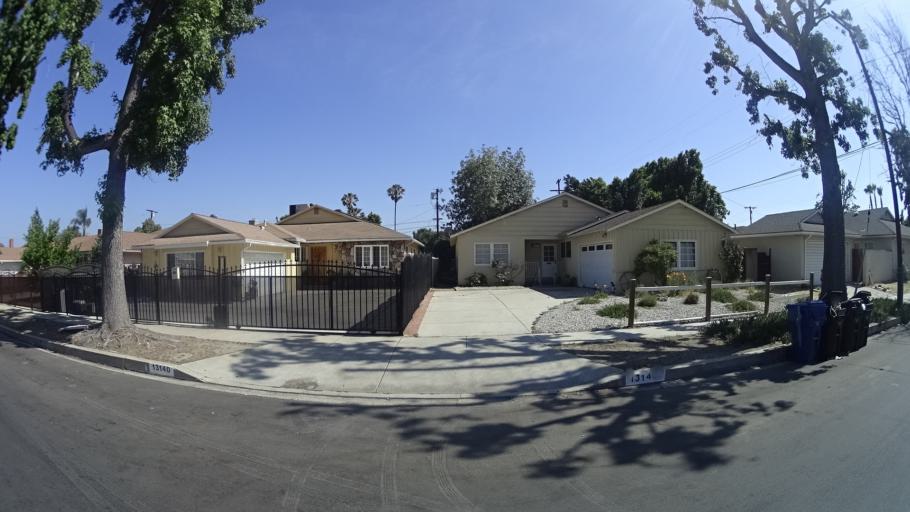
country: US
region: California
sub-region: Los Angeles County
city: Van Nuys
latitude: 34.1958
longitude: -118.4196
